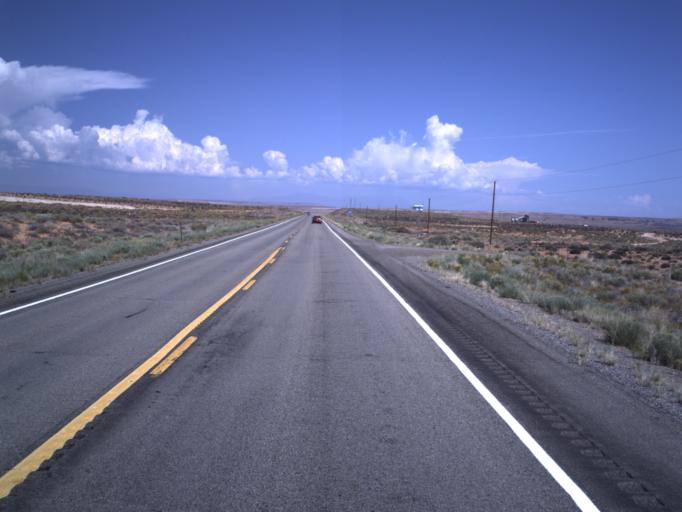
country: US
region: Utah
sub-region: San Juan County
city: Blanding
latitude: 37.0794
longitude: -109.5480
